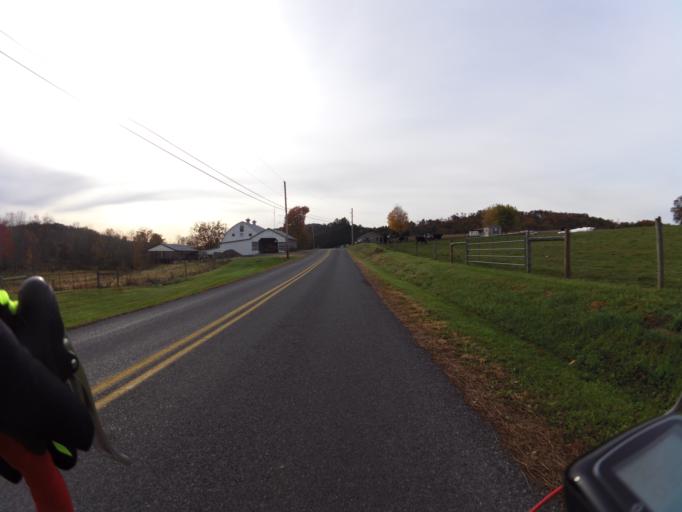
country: US
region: Pennsylvania
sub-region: Union County
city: New Columbia
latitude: 41.0390
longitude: -76.9478
